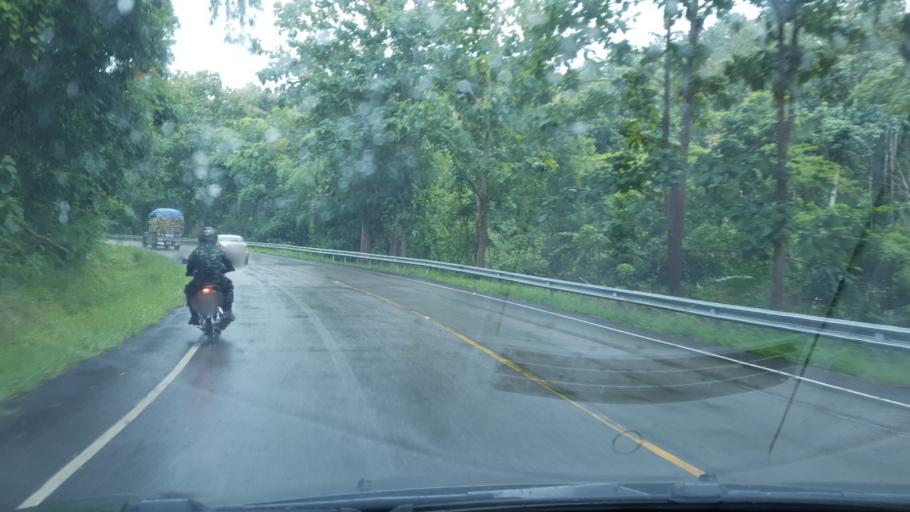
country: TH
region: Mae Hong Son
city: Mae La Noi
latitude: 18.5569
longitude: 97.9255
